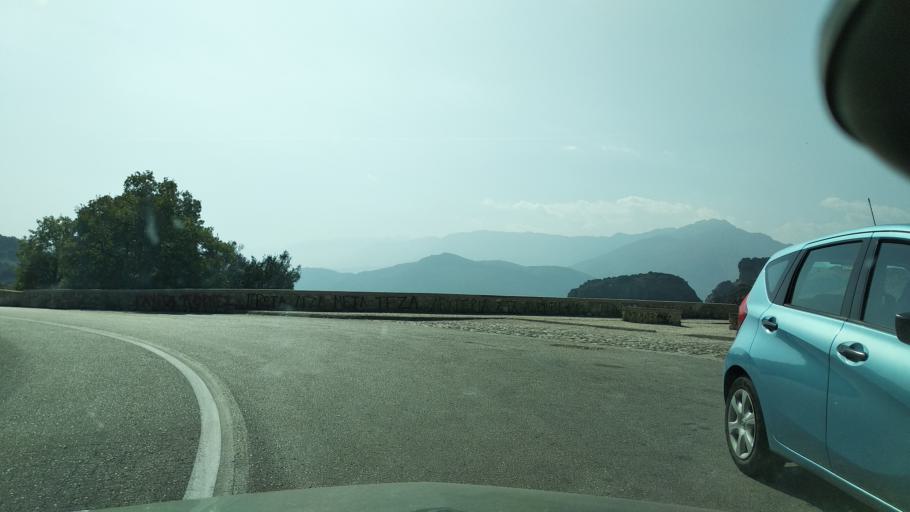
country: GR
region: Thessaly
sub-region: Trikala
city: Kalampaka
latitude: 39.7194
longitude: 21.6373
